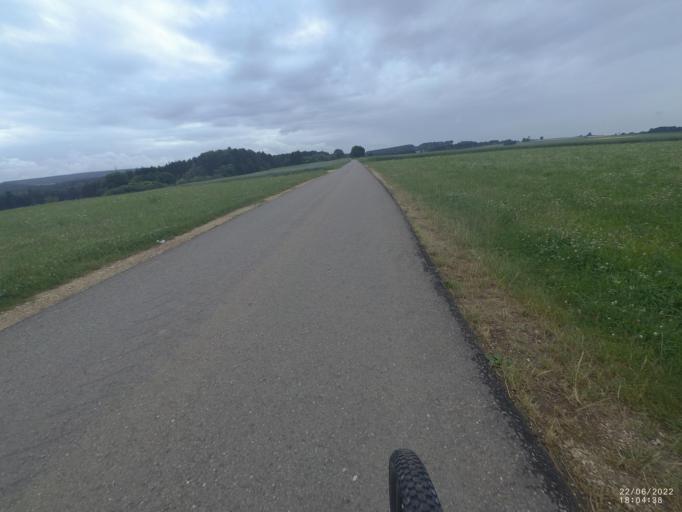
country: DE
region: Baden-Wuerttemberg
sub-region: Regierungsbezirk Stuttgart
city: Gerstetten
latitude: 48.6230
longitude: 10.0036
